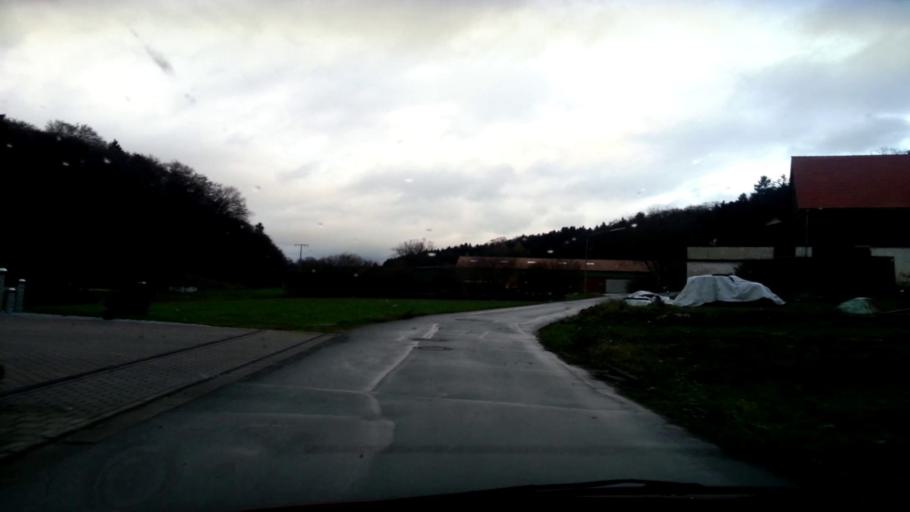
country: DE
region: Bavaria
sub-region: Upper Franconia
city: Aufsess
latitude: 49.9288
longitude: 11.2052
